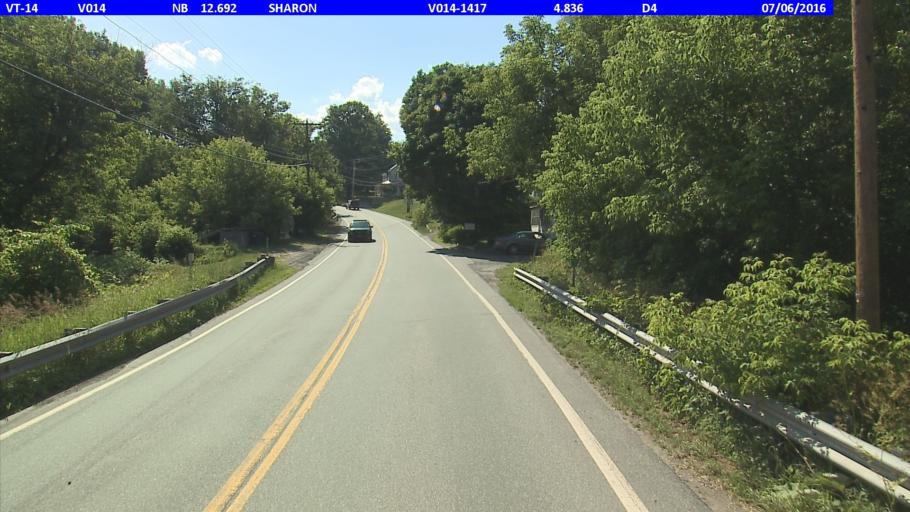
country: US
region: Vermont
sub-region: Windsor County
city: Woodstock
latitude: 43.7841
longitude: -72.4504
